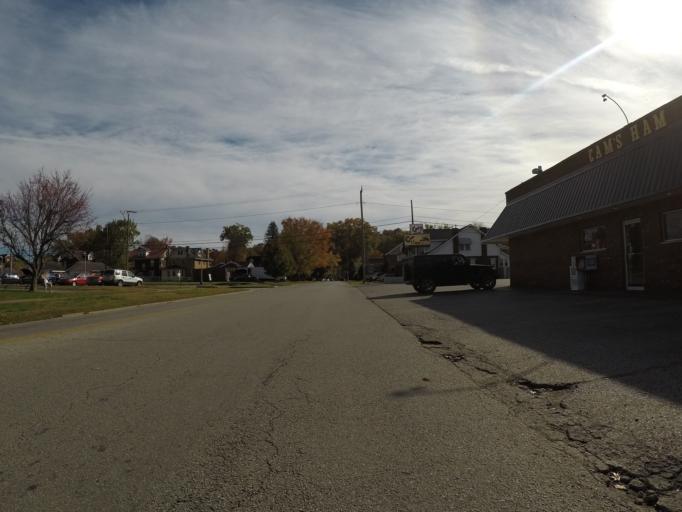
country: US
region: West Virginia
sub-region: Cabell County
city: Huntington
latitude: 38.4125
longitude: -82.4558
